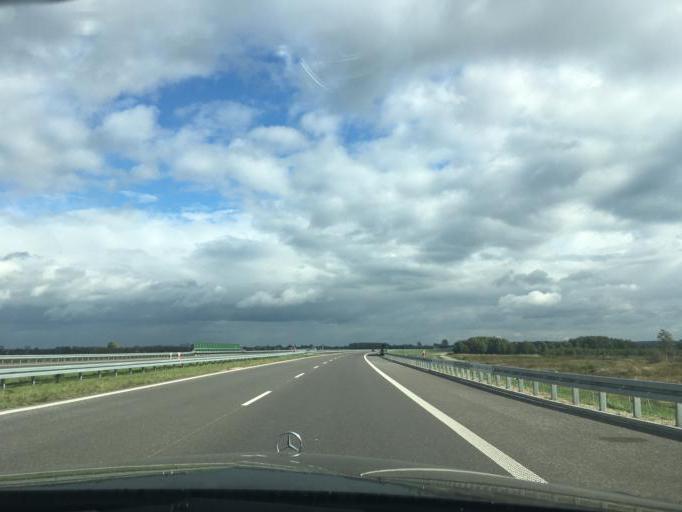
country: PL
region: Subcarpathian Voivodeship
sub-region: Powiat rzeszowski
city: Wolka Podlesna
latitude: 50.0959
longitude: 22.1147
